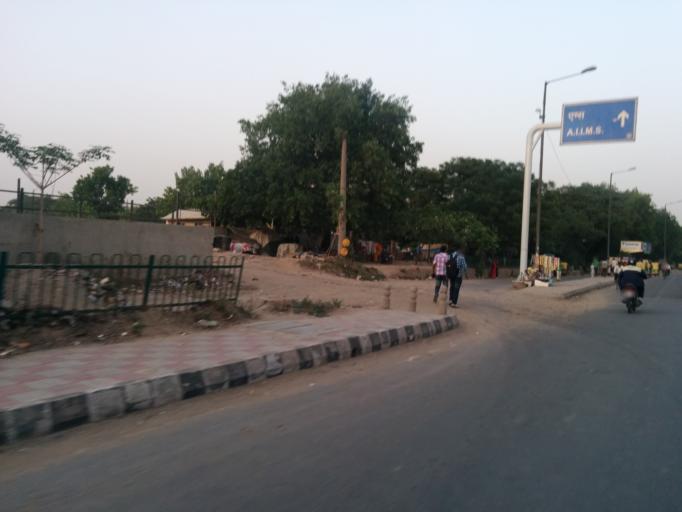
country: IN
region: NCT
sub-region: New Delhi
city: New Delhi
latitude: 28.5700
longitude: 77.2001
